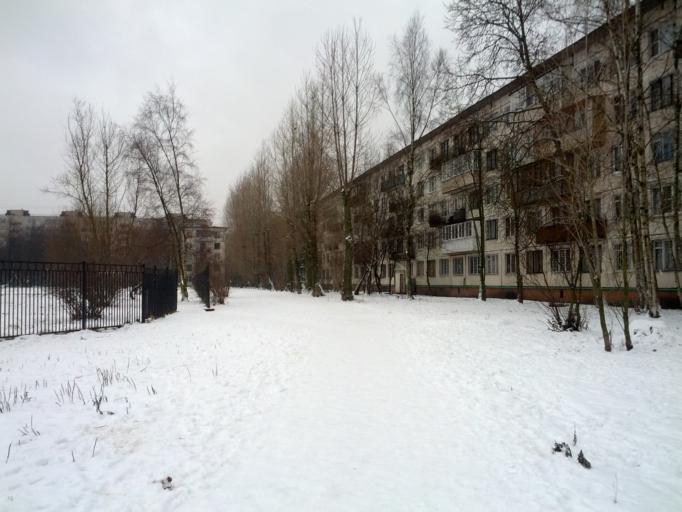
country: RU
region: St.-Petersburg
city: Krasnogvargeisky
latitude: 59.9085
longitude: 30.4766
